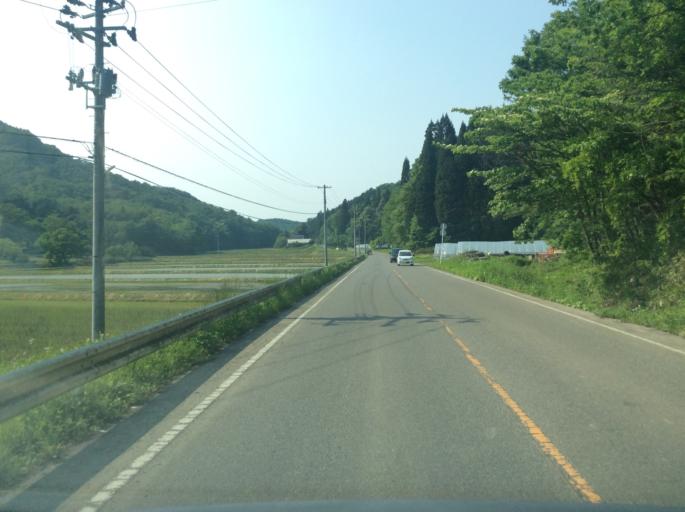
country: JP
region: Tochigi
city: Kuroiso
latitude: 37.0633
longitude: 140.2323
